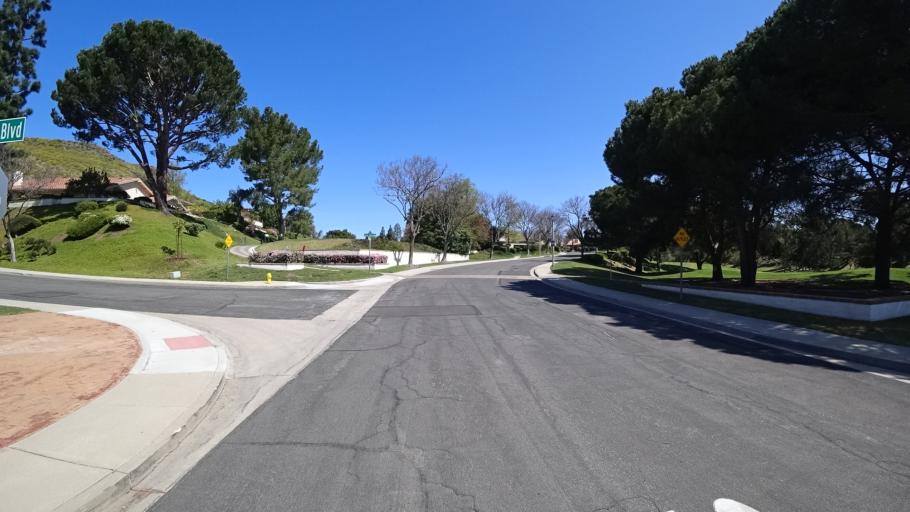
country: US
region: California
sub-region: Ventura County
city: Moorpark
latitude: 34.2315
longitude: -118.8550
